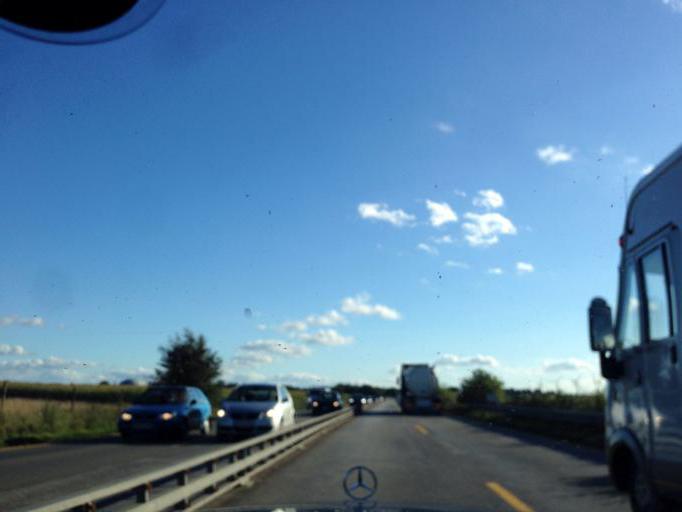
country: DE
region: Schleswig-Holstein
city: Schonbek
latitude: 54.1538
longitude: 9.9645
